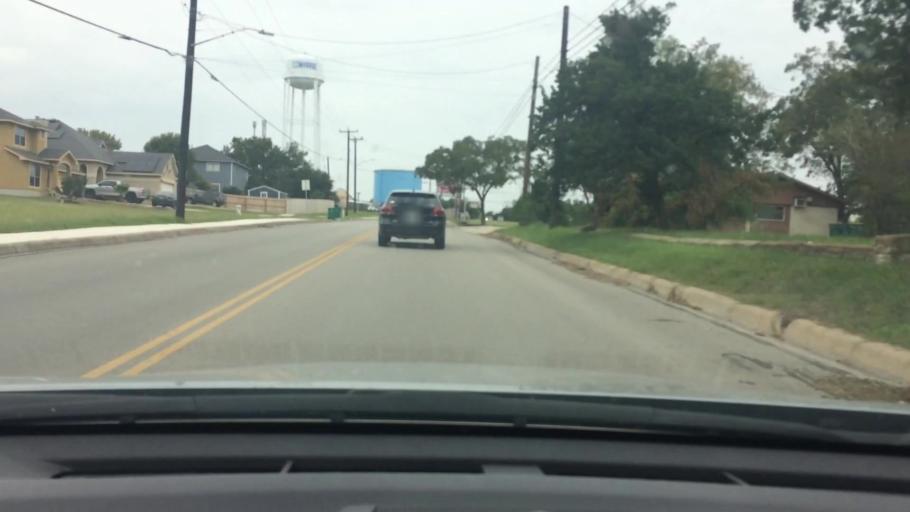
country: US
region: Texas
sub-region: Bexar County
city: Converse
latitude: 29.5244
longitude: -98.3214
